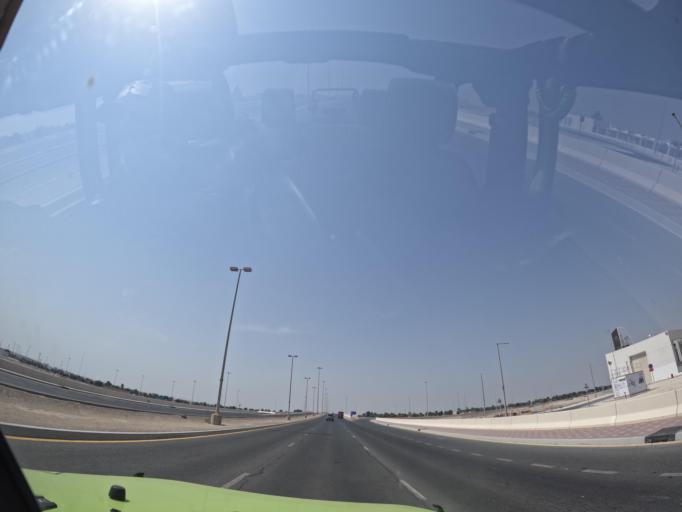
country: AE
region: Abu Dhabi
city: Abu Dhabi
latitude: 24.3379
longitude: 54.6402
